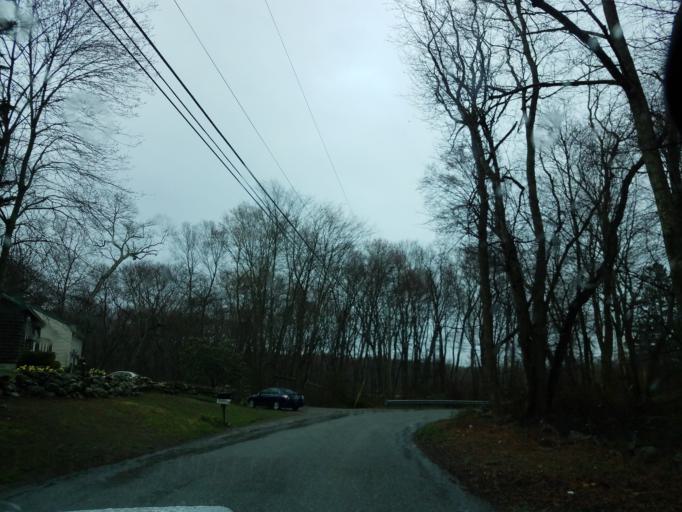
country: US
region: Rhode Island
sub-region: Washington County
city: Ashaway
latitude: 41.4377
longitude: -71.8123
